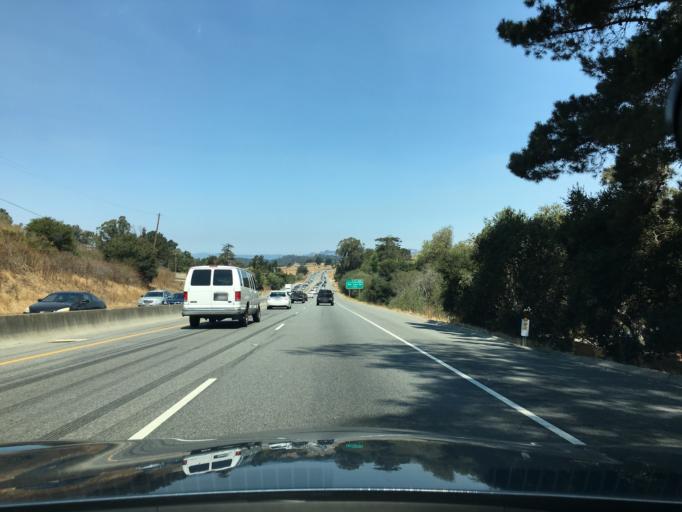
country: US
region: California
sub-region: San Benito County
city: Aromas
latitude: 36.8407
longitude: -121.6325
